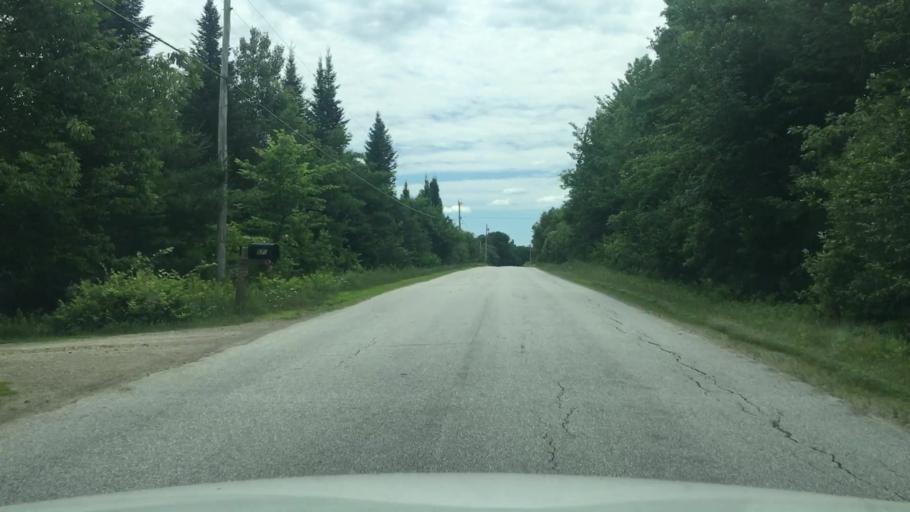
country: US
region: Maine
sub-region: Waldo County
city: Searsmont
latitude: 44.4537
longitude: -69.2556
